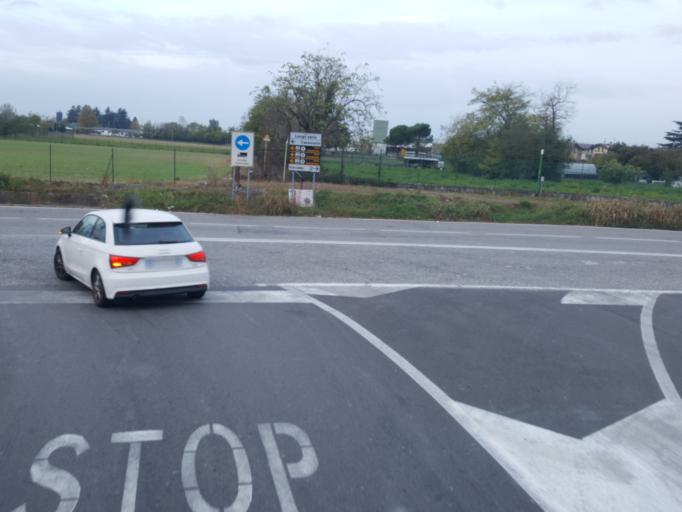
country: IT
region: Lombardy
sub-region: Provincia di Bergamo
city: Grassobbio
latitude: 45.6466
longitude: 9.7308
